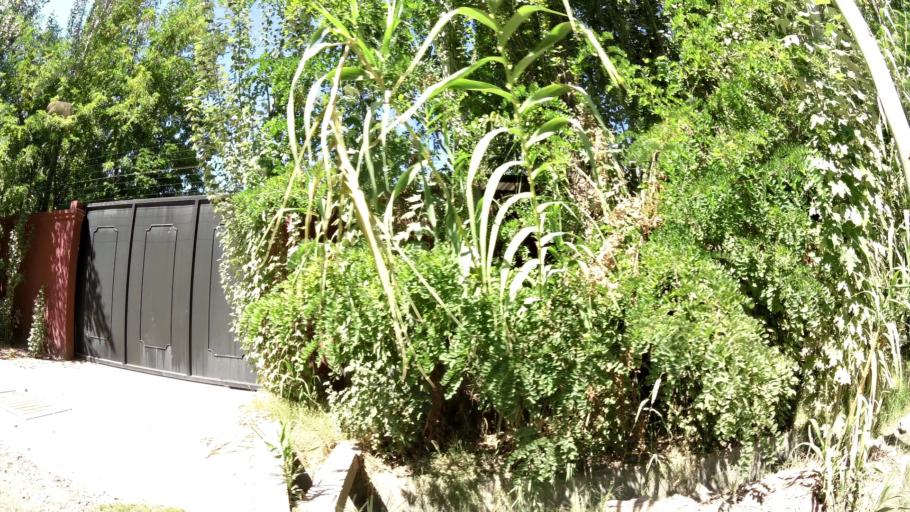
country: AR
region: Mendoza
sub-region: Departamento de Godoy Cruz
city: Godoy Cruz
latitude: -32.9719
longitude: -68.8692
